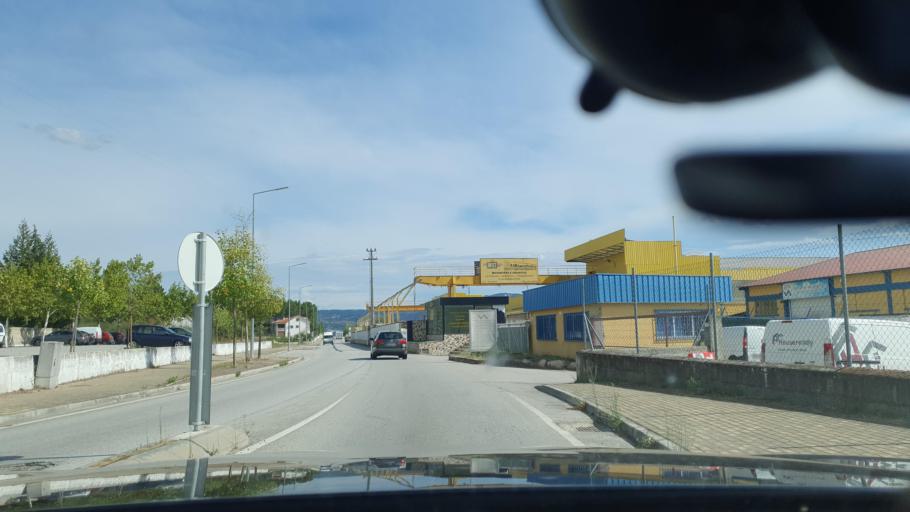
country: PT
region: Vila Real
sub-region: Chaves
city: Chaves
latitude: 41.7690
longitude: -7.4846
